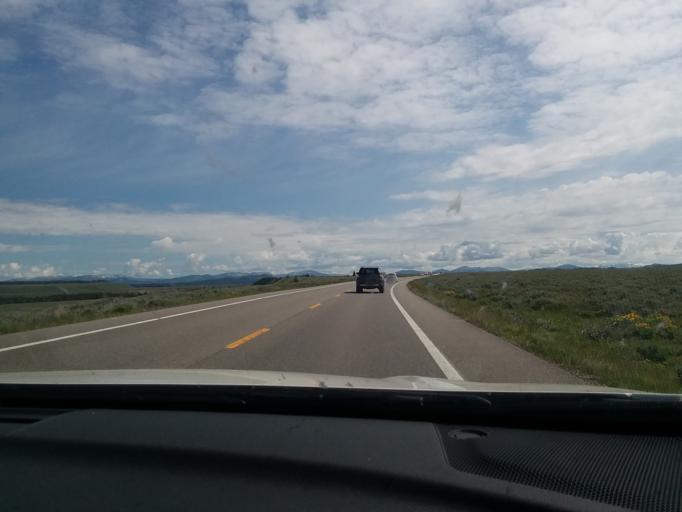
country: US
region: Wyoming
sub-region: Teton County
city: Jackson
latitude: 43.7232
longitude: -110.6563
